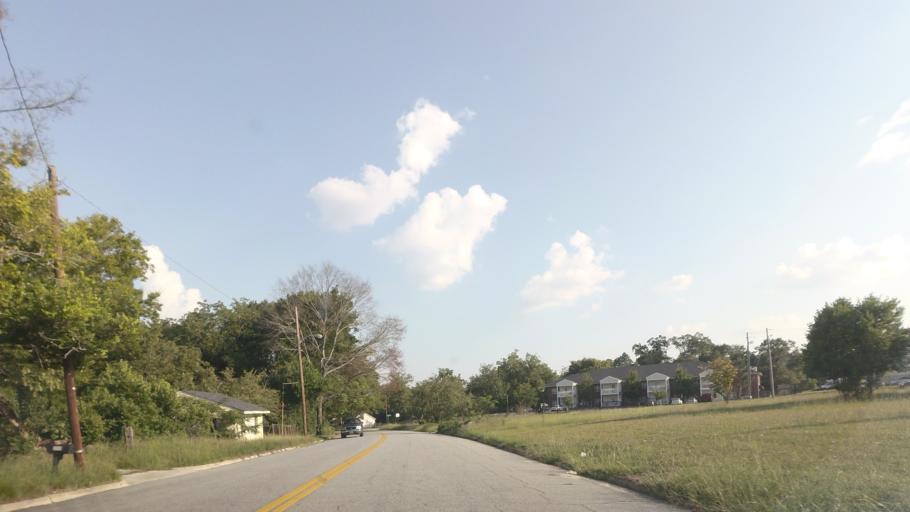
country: US
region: Georgia
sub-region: Bibb County
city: Macon
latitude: 32.8425
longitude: -83.6825
